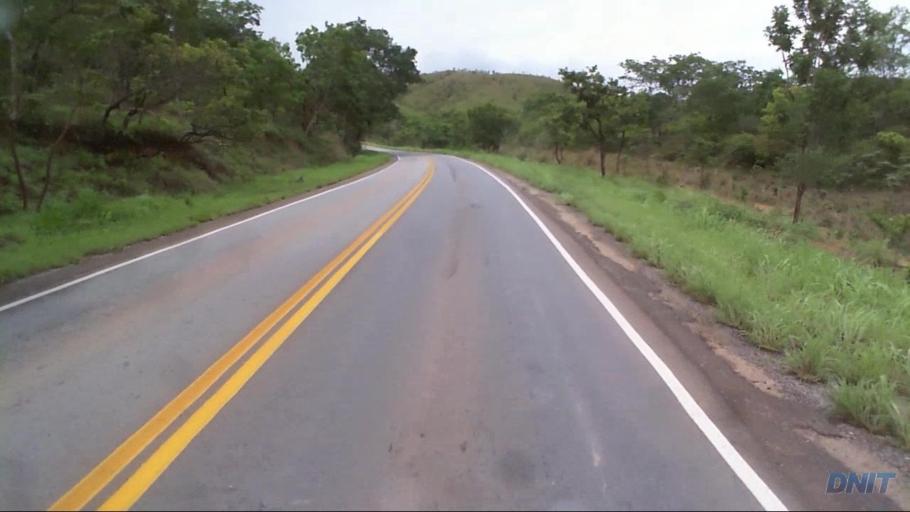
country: BR
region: Goias
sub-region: Padre Bernardo
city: Padre Bernardo
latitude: -15.4564
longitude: -48.2148
